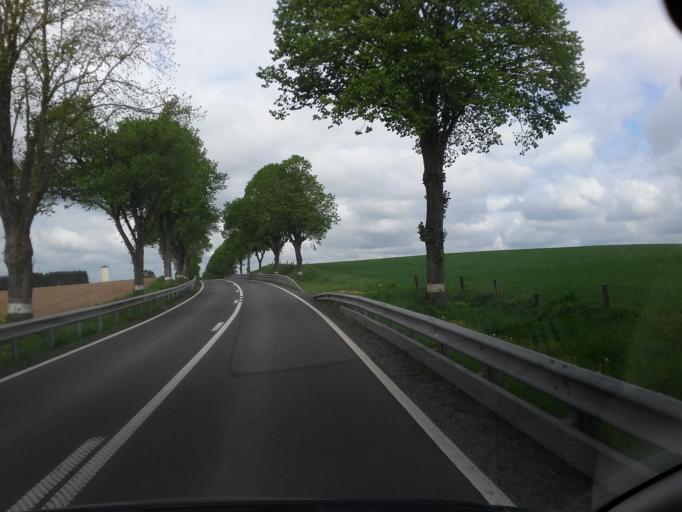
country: BE
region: Wallonia
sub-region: Province du Luxembourg
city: Neufchateau
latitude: 49.8435
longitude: 5.3935
